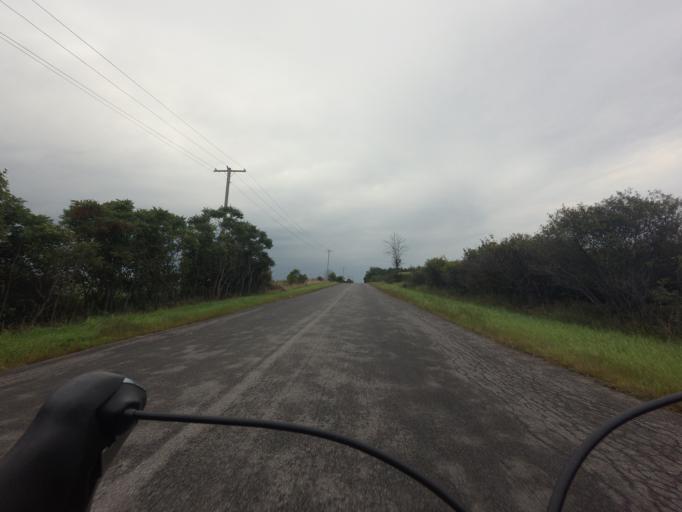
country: CA
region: Ontario
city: Bells Corners
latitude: 45.1448
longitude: -75.7638
